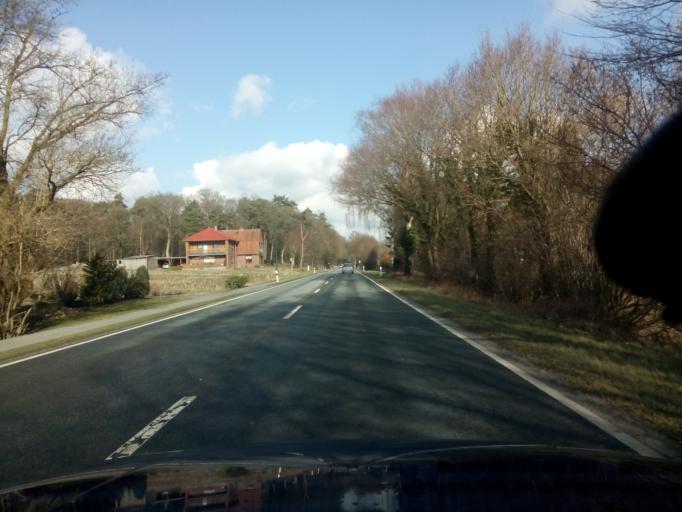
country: DE
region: Lower Saxony
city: Hambergen
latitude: 53.2783
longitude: 8.8218
